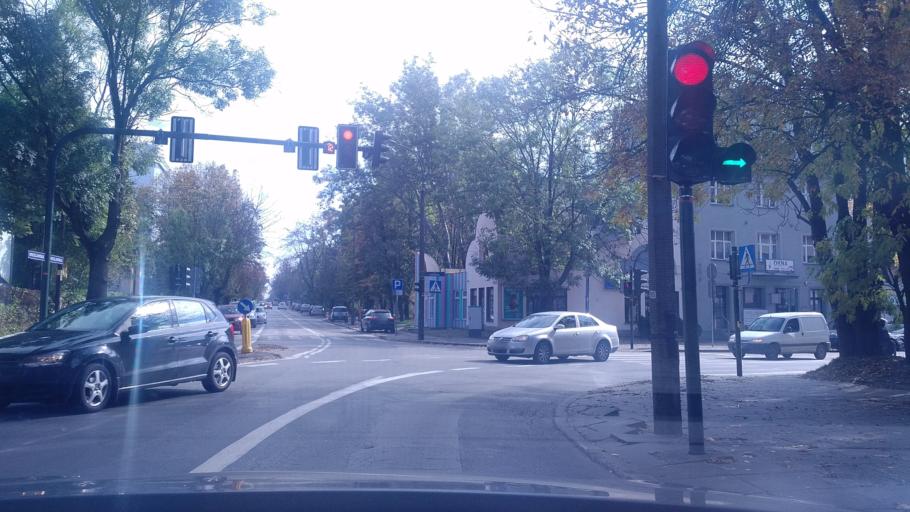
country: PL
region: Lesser Poland Voivodeship
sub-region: Krakow
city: Krakow
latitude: 50.0804
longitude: 19.9186
